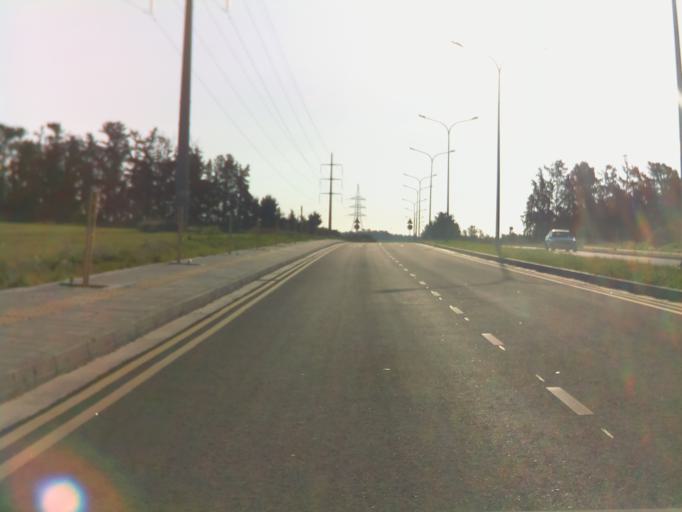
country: CY
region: Pafos
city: Paphos
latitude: 34.7371
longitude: 32.4574
